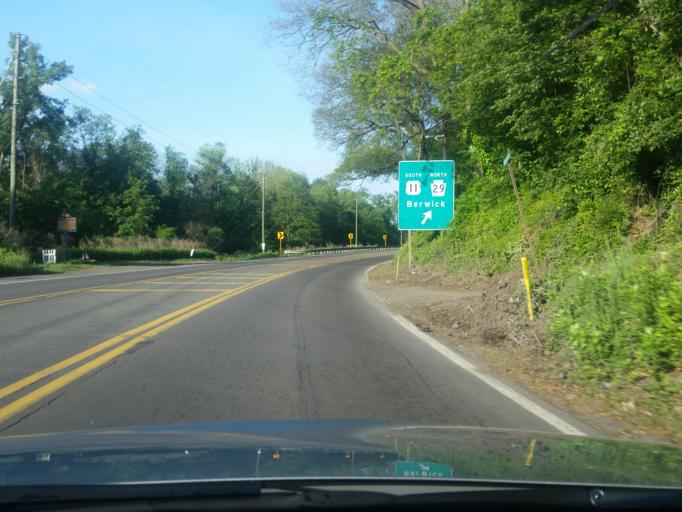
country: US
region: Pennsylvania
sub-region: Luzerne County
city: Plymouth
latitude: 41.2269
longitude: -75.9743
